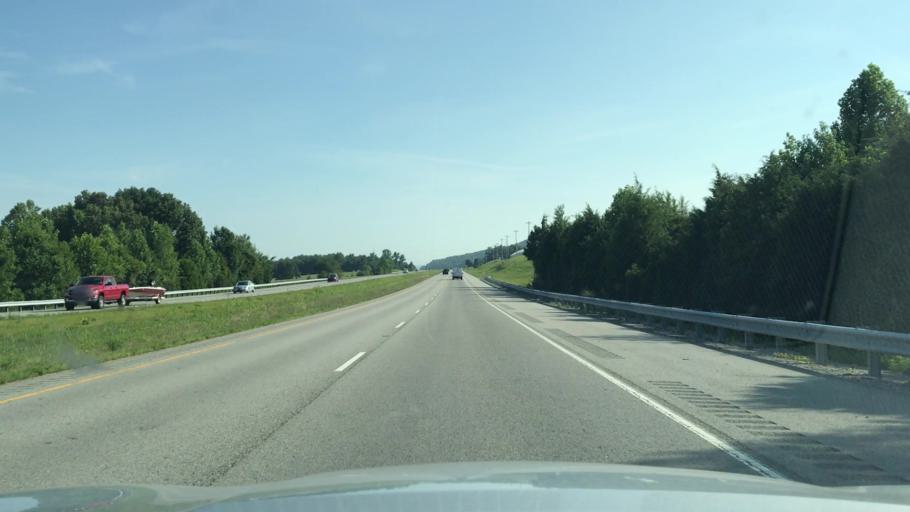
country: US
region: Tennessee
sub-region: Overton County
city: Livingston
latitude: 36.2882
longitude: -85.3737
